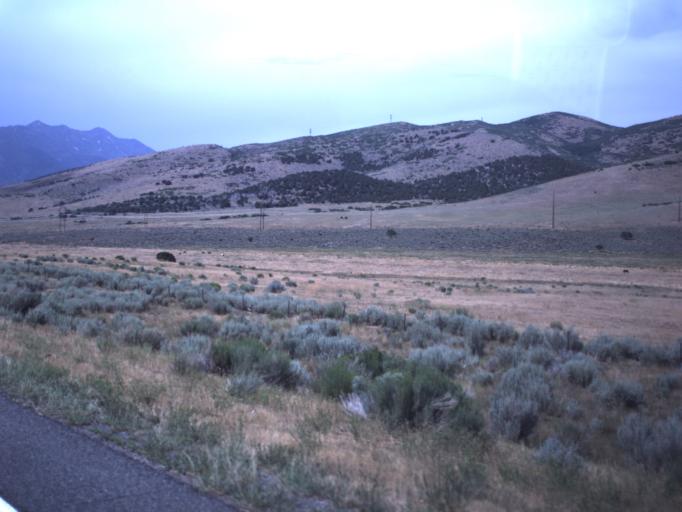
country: US
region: Utah
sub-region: Sanpete County
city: Fountain Green
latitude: 39.6854
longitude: -111.6780
